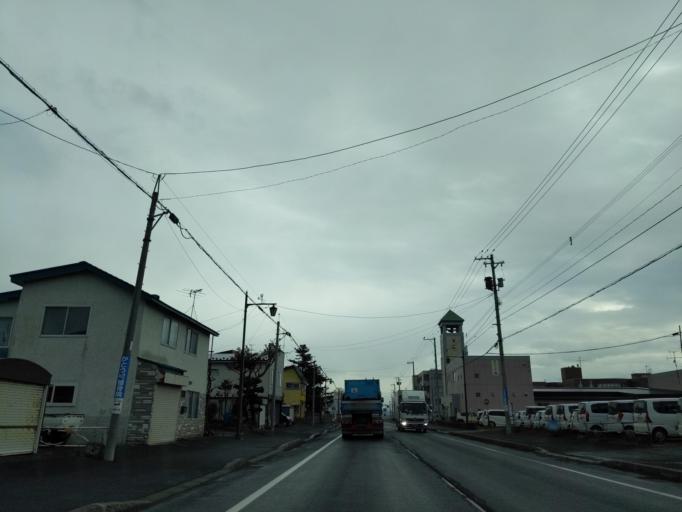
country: JP
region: Hokkaido
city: Ebetsu
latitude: 43.0656
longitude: 141.6532
